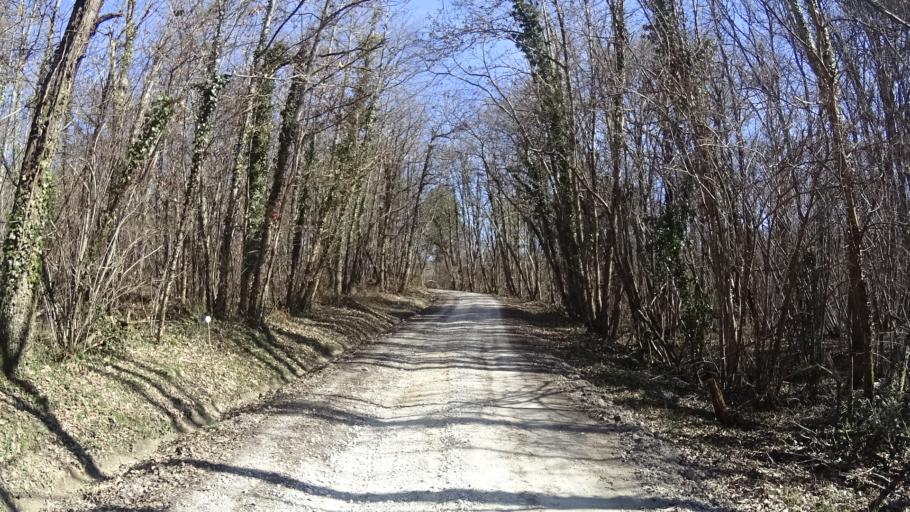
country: FR
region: Aquitaine
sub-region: Departement de la Dordogne
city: Riberac
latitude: 45.1997
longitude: 0.3137
